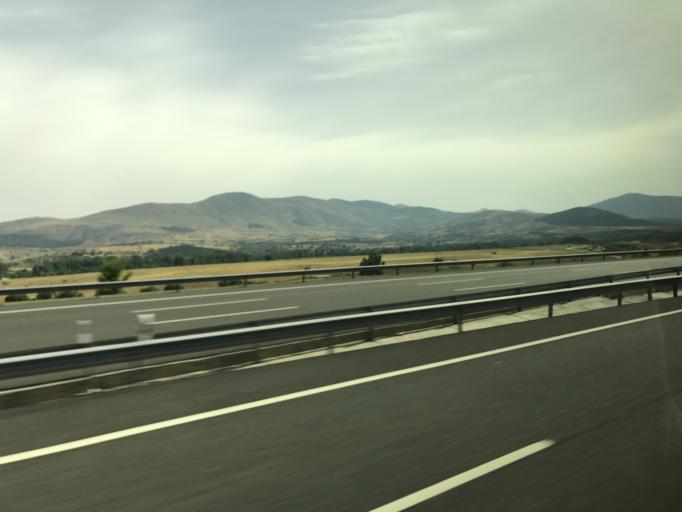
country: ES
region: Castille and Leon
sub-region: Provincia de Segovia
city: Vegas de Matute
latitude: 40.7389
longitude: -4.2196
